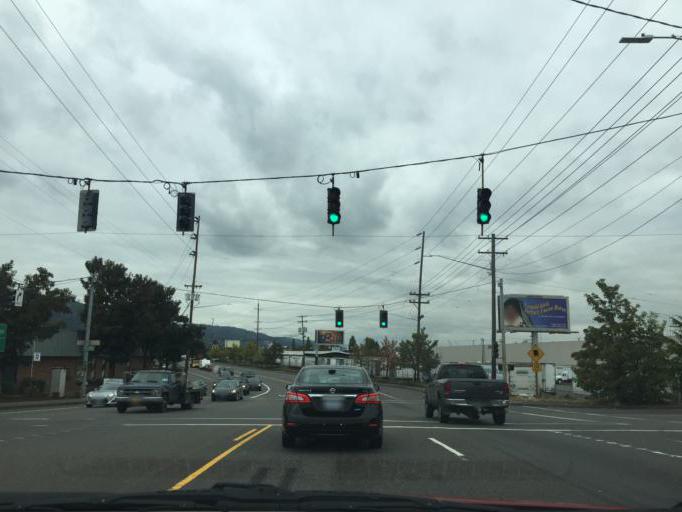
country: US
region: Oregon
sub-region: Multnomah County
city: Portland
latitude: 45.5437
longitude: -122.7023
